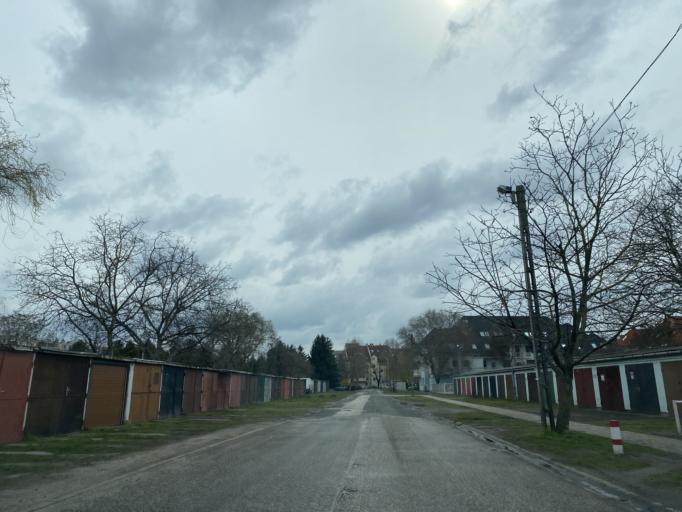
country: HU
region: Csongrad
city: Szeged
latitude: 46.2668
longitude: 20.1454
